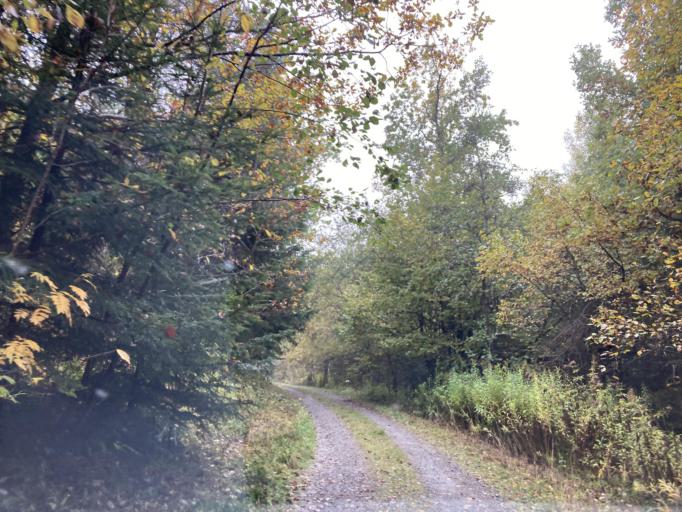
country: DE
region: Baden-Wuerttemberg
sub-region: Tuebingen Region
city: Rottenburg
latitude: 48.5099
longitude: 8.9094
